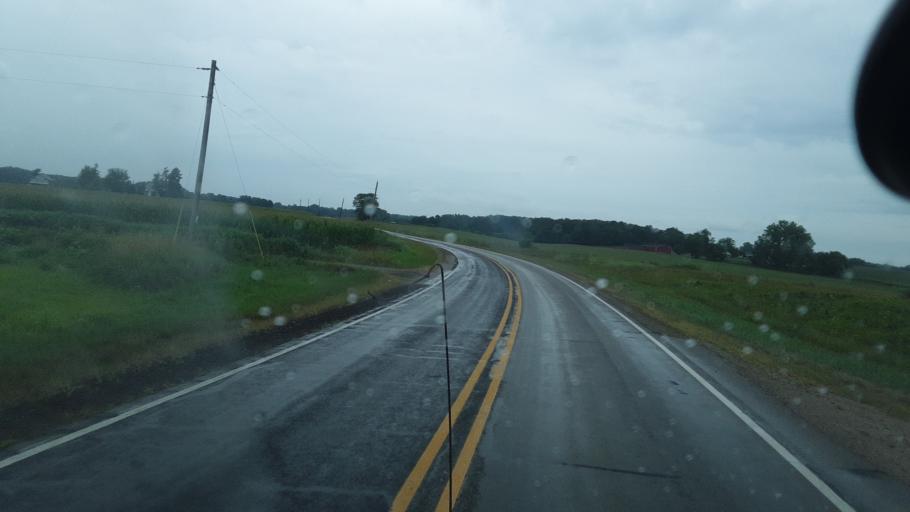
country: US
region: Indiana
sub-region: Steuben County
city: Hamilton
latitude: 41.5589
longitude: -84.8113
